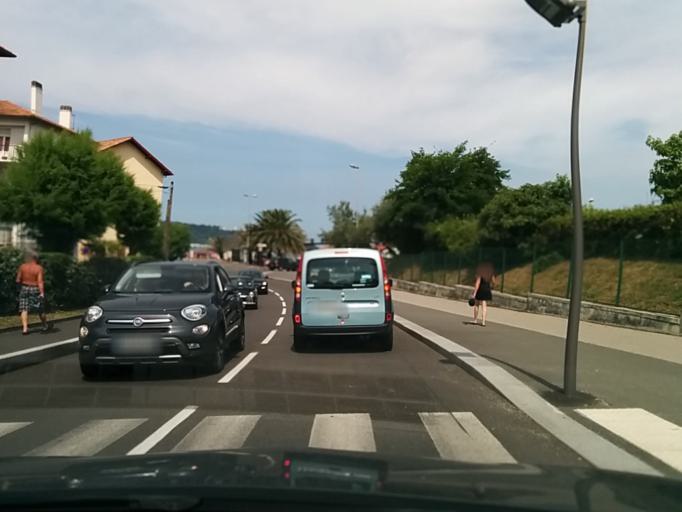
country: FR
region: Aquitaine
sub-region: Departement des Pyrenees-Atlantiques
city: Hendaye
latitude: 43.3751
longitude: -1.7611
